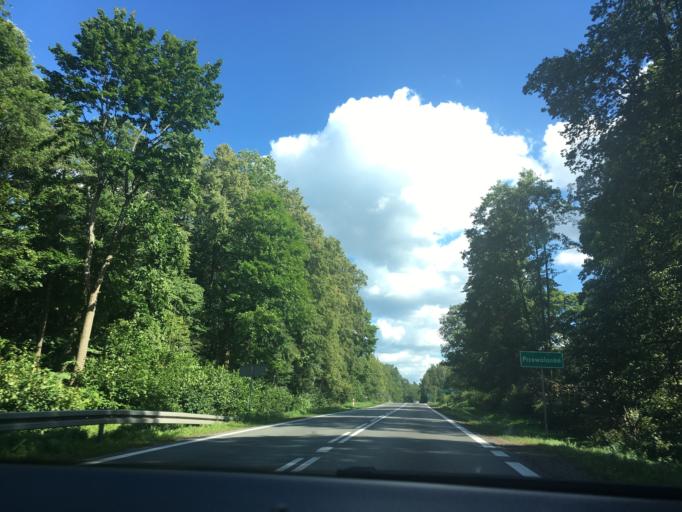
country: PL
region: Podlasie
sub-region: Powiat bialostocki
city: Wasilkow
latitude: 53.3262
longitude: 23.1210
